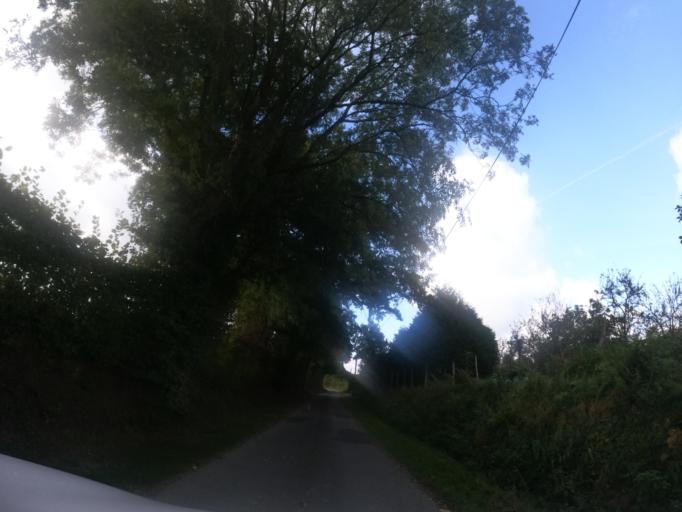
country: FR
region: Poitou-Charentes
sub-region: Departement des Deux-Sevres
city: Courlay
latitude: 46.7801
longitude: -0.6031
